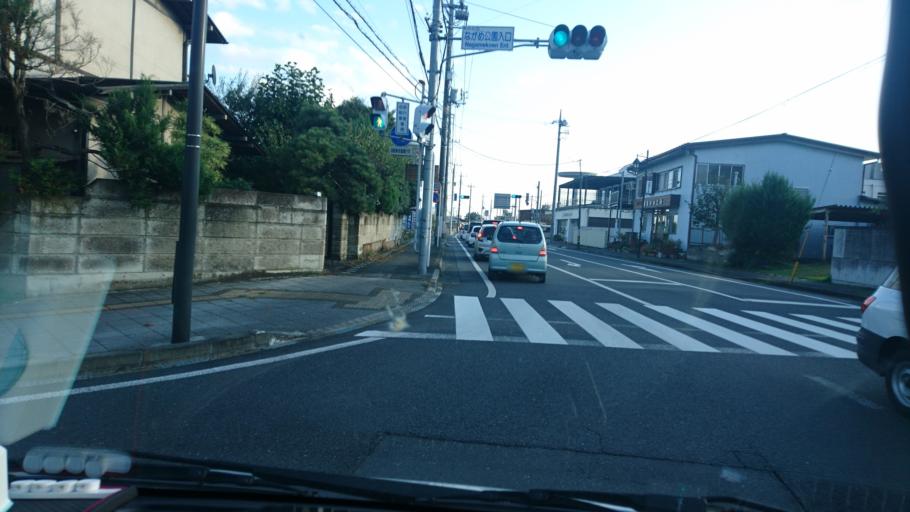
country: JP
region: Gunma
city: Omamacho-omama
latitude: 36.4365
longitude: 139.2768
